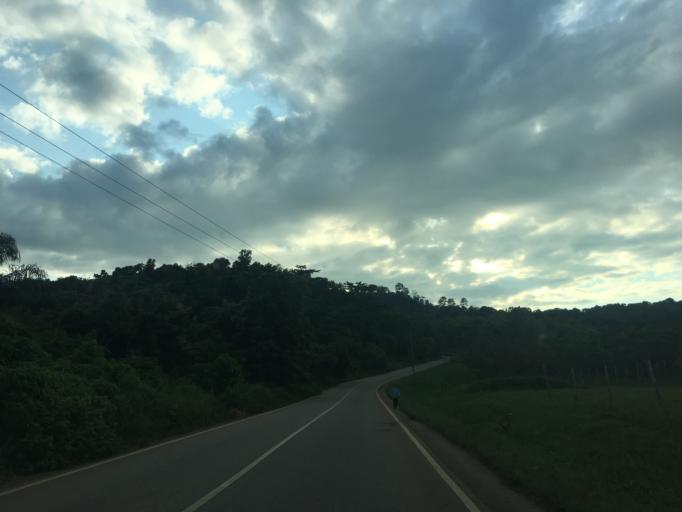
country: GH
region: Western
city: Bibiani
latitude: 6.4641
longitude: -2.3270
